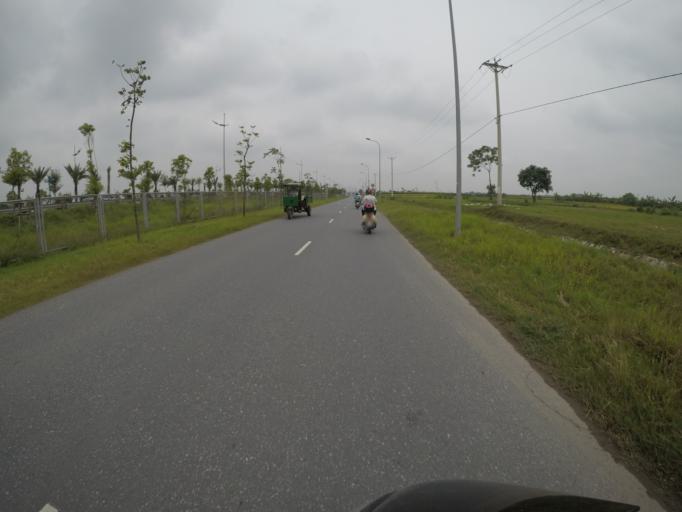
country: VN
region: Ha Noi
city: Dong Anh
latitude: 21.1817
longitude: 105.8285
